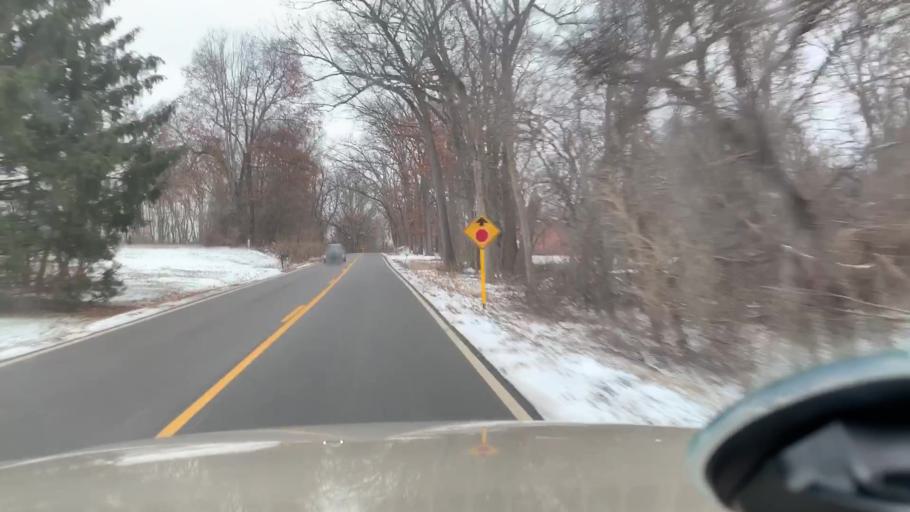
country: US
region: Michigan
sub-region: Jackson County
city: Spring Arbor
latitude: 42.2025
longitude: -84.5309
